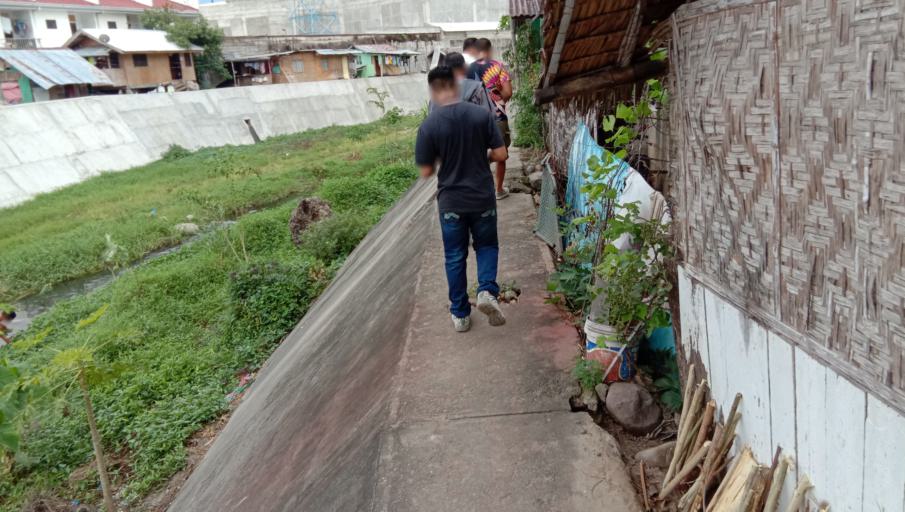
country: PH
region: Central Visayas
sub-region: Province of Negros Oriental
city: Dumaguete
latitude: 9.3020
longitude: 123.3016
